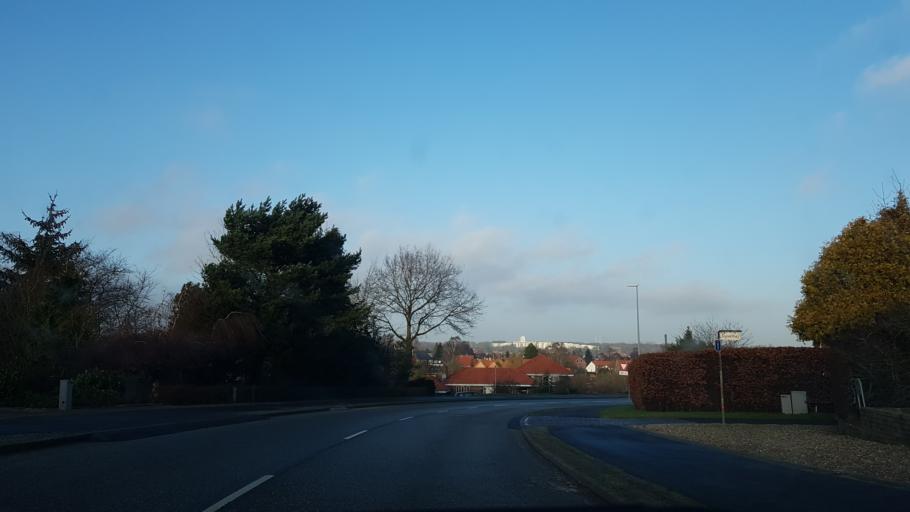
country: DK
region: South Denmark
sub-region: Haderslev Kommune
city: Haderslev
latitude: 55.2390
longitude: 9.4988
